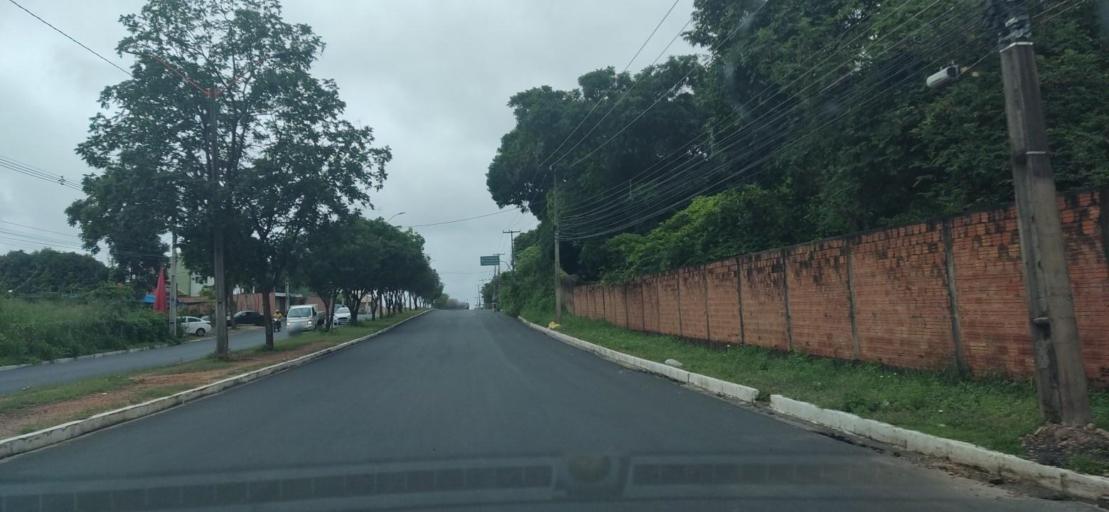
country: BR
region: Piaui
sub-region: Teresina
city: Teresina
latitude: -5.0637
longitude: -42.7490
